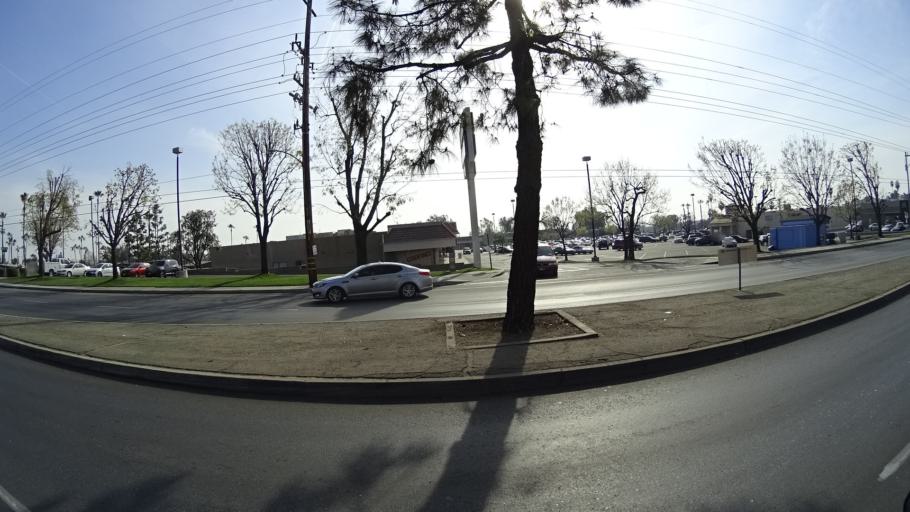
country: US
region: California
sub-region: Kern County
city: Oildale
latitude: 35.3977
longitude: -118.9660
